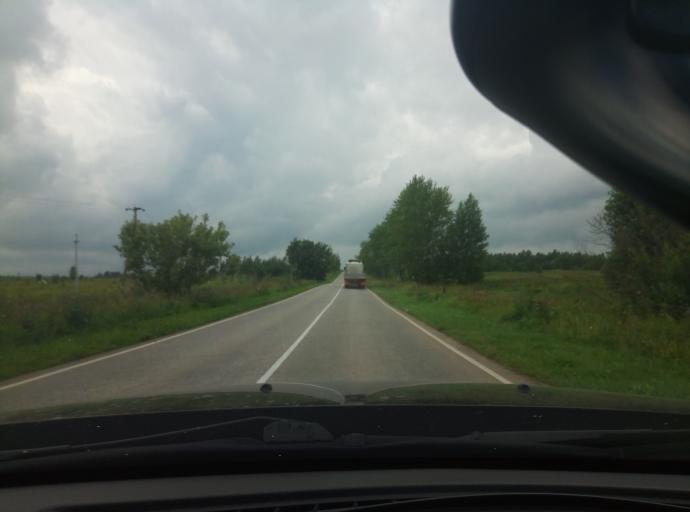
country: RU
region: Tula
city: Priupskiy
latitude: 53.9734
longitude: 37.7409
